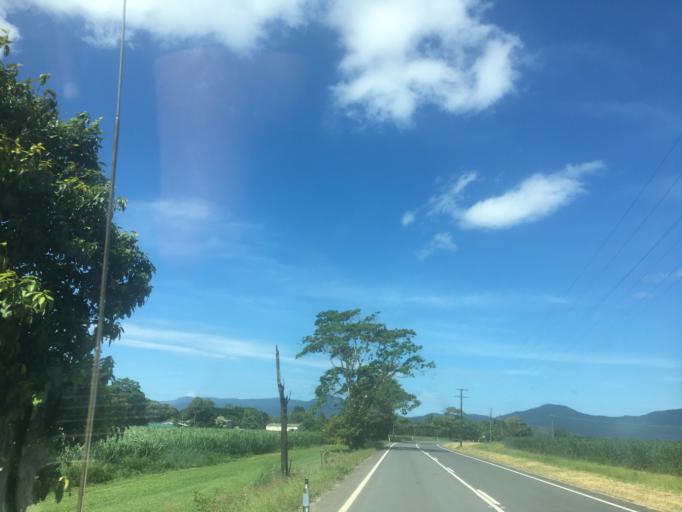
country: AU
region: Queensland
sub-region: Cairns
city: Woree
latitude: -17.0645
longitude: 145.7553
